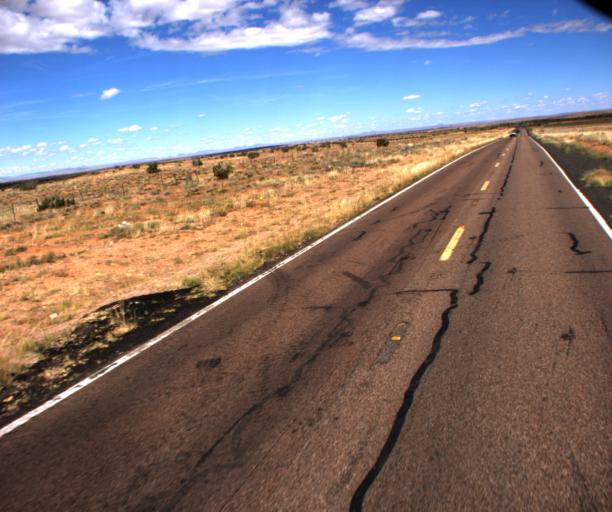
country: US
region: Arizona
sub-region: Navajo County
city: Holbrook
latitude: 34.7428
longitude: -110.2681
